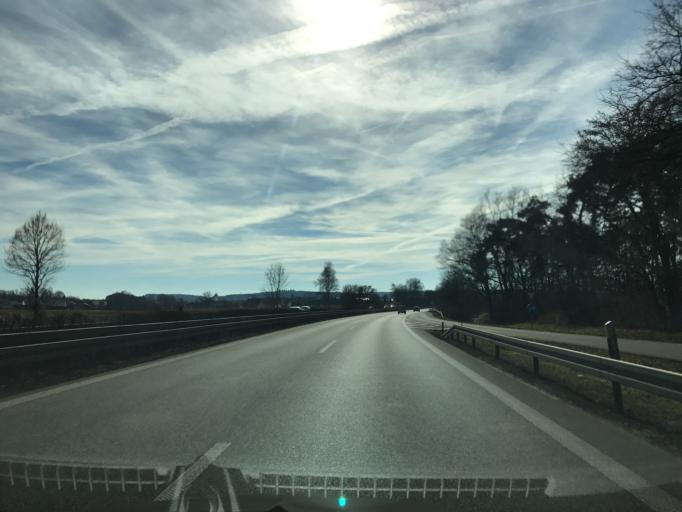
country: DE
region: Baden-Wuerttemberg
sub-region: Tuebingen Region
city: Maselheim
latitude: 48.1641
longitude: 9.8585
